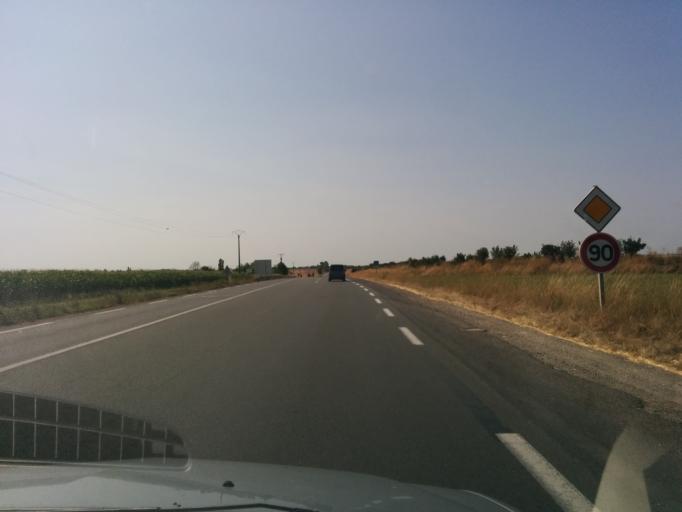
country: FR
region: Poitou-Charentes
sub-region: Departement de la Vienne
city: Neuville-de-Poitou
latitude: 46.6953
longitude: 0.2508
